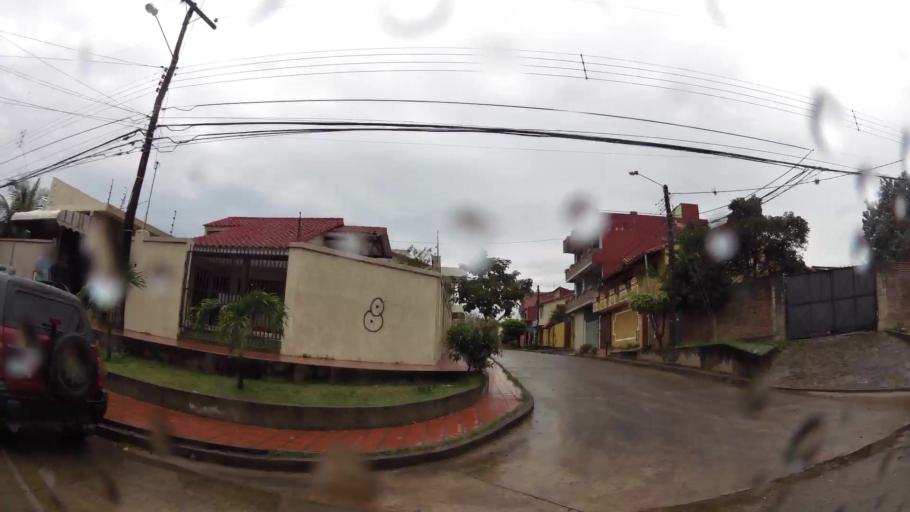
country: BO
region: Santa Cruz
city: Santa Cruz de la Sierra
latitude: -17.8162
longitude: -63.2014
